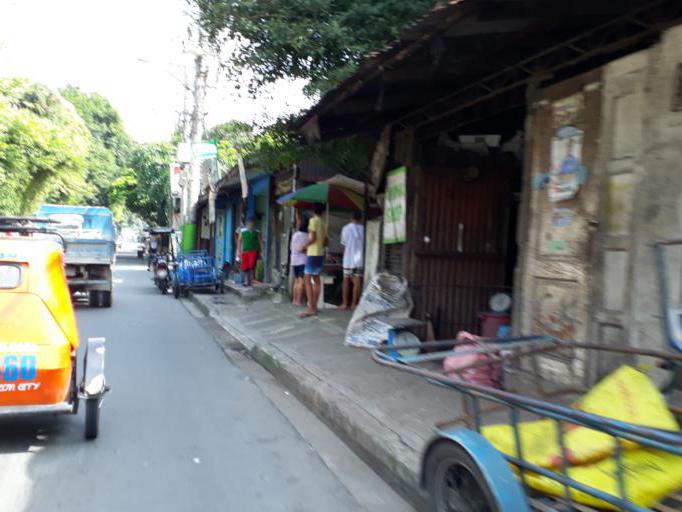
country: PH
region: Calabarzon
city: Bagong Pagasa
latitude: 14.6696
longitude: 121.0064
